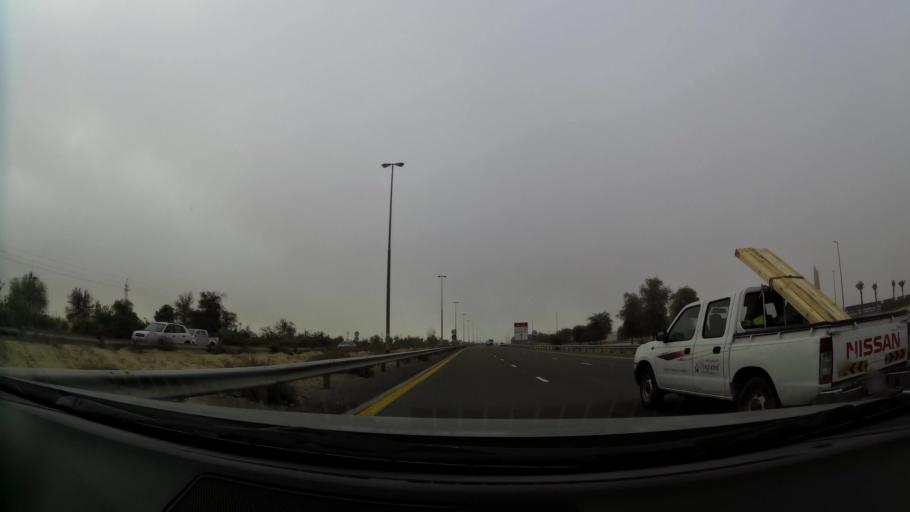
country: AE
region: Dubai
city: Dubai
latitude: 25.0518
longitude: 55.4255
